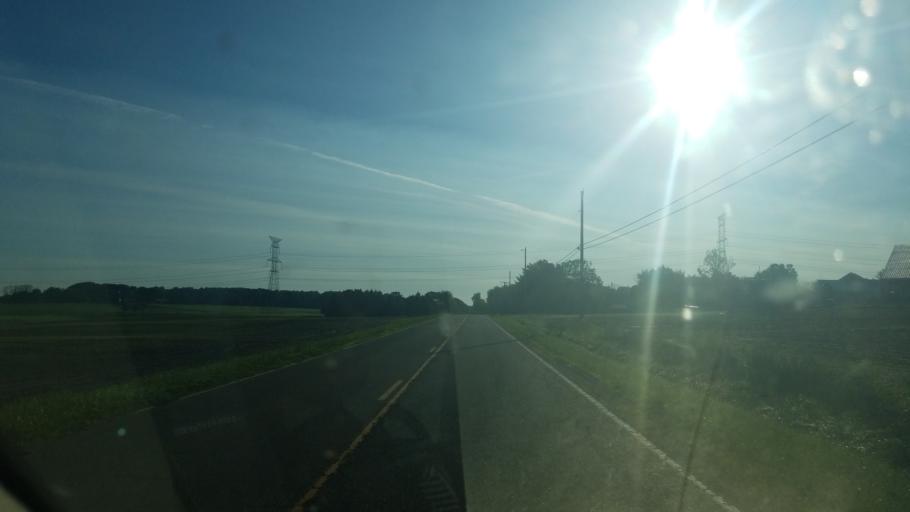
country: US
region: Ohio
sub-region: Columbiana County
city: Salem
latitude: 40.8831
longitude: -80.9061
